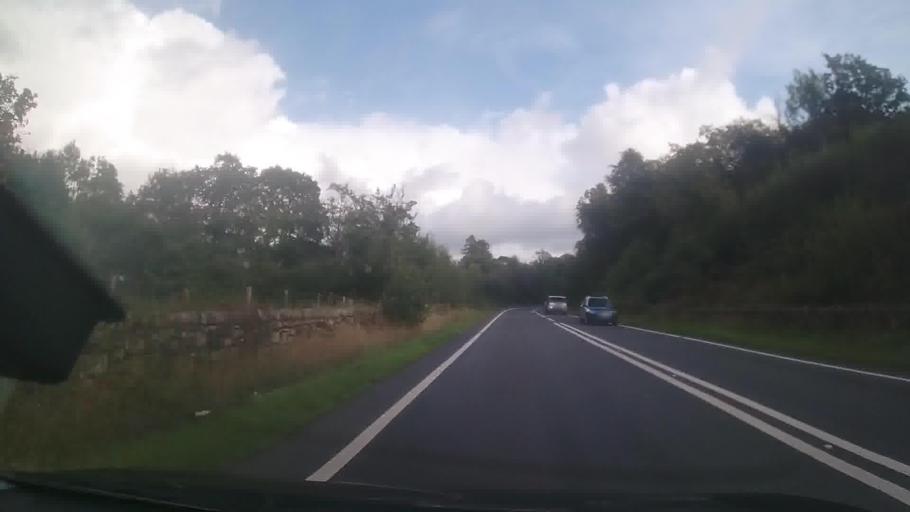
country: GB
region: Wales
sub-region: Gwynedd
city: Dolgellau
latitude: 52.7487
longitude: -3.8447
